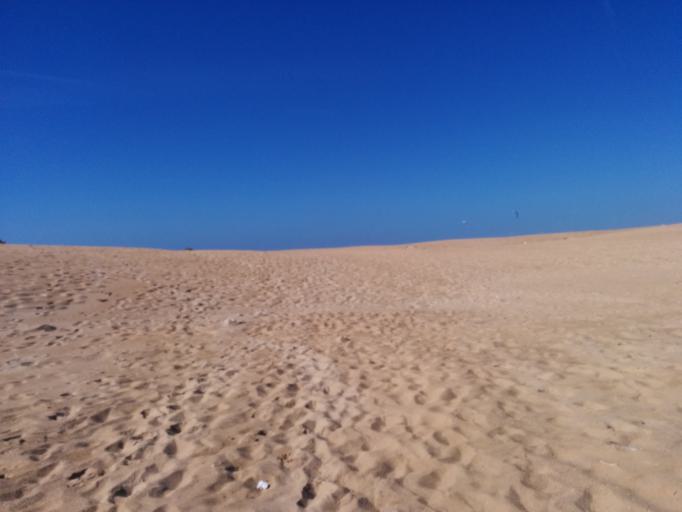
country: PT
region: Faro
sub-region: Vila do Bispo
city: Vila do Bispo
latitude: 37.1967
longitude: -8.9020
